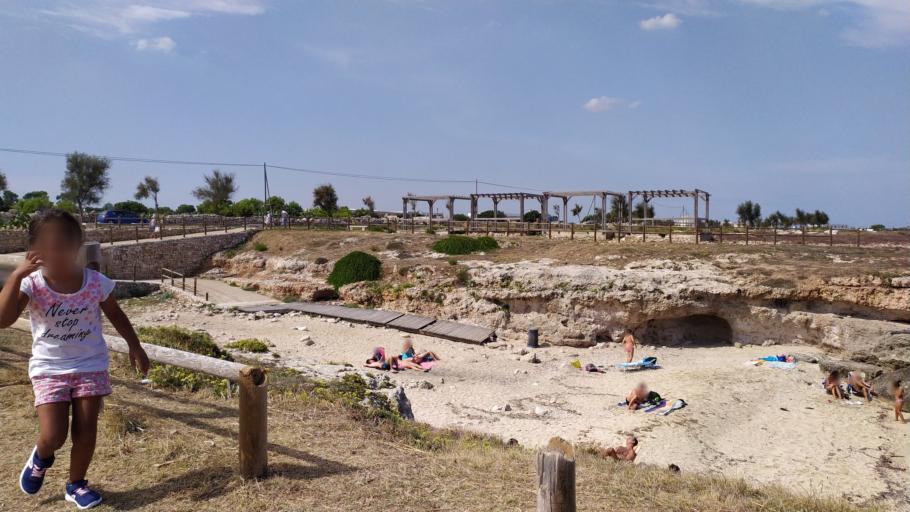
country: IT
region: Apulia
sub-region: Provincia di Bari
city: Monopoli
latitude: 40.9641
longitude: 17.2859
